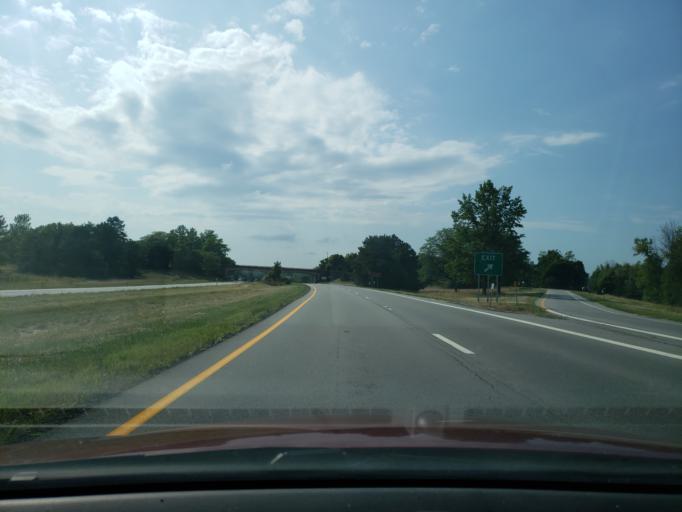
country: US
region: New York
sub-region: Monroe County
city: Irondequoit
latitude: 43.2552
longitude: -77.6258
